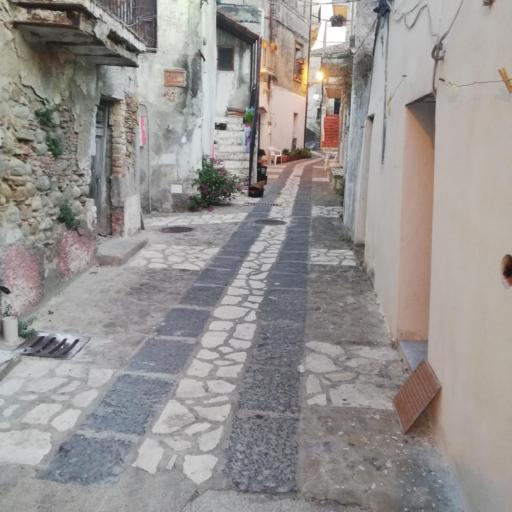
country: IT
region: Calabria
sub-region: Provincia di Cosenza
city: Cariati
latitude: 39.4957
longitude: 16.9467
